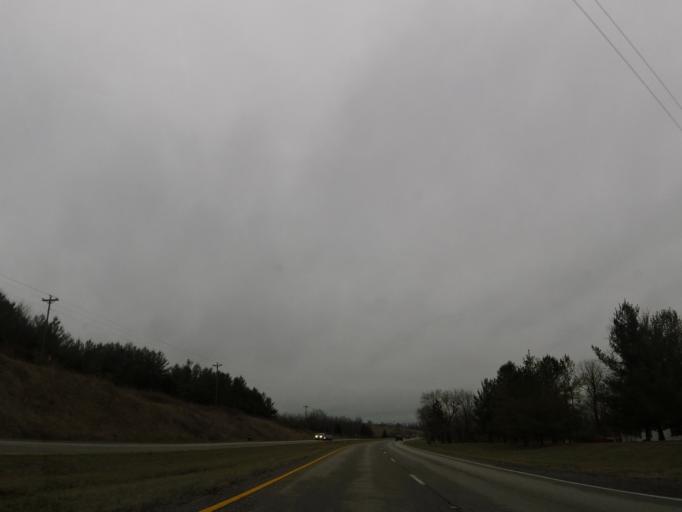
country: US
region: Kentucky
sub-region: Boyle County
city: Danville
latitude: 37.6151
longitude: -84.7295
